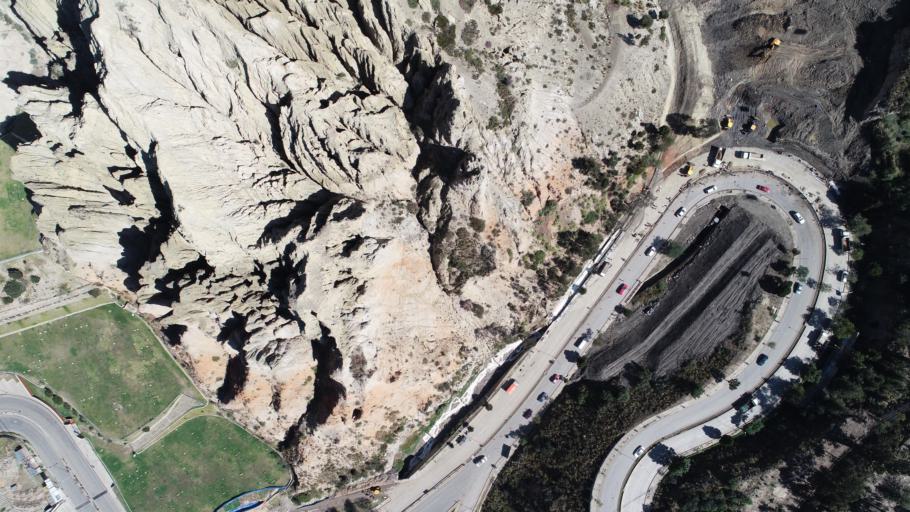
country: BO
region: La Paz
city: La Paz
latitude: -16.5197
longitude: -68.1193
